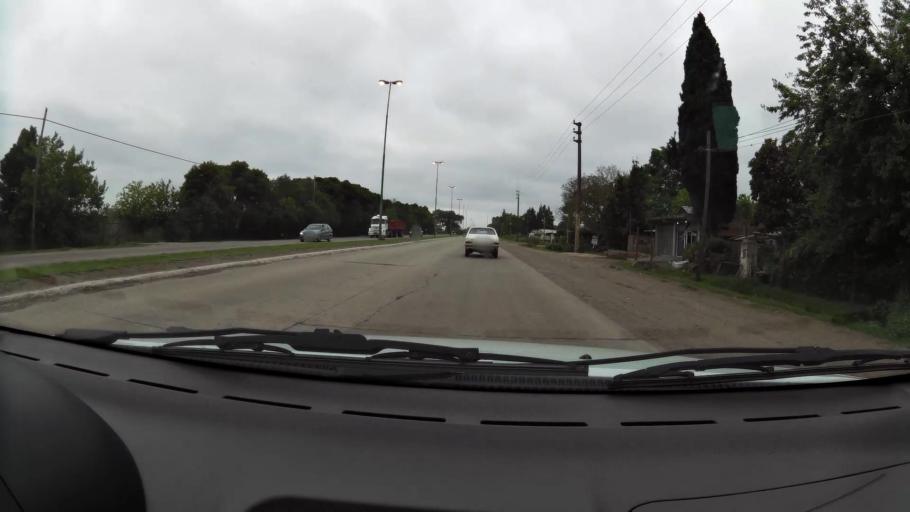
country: AR
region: Buenos Aires
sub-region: Partido de La Plata
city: La Plata
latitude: -35.0269
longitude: -58.0829
